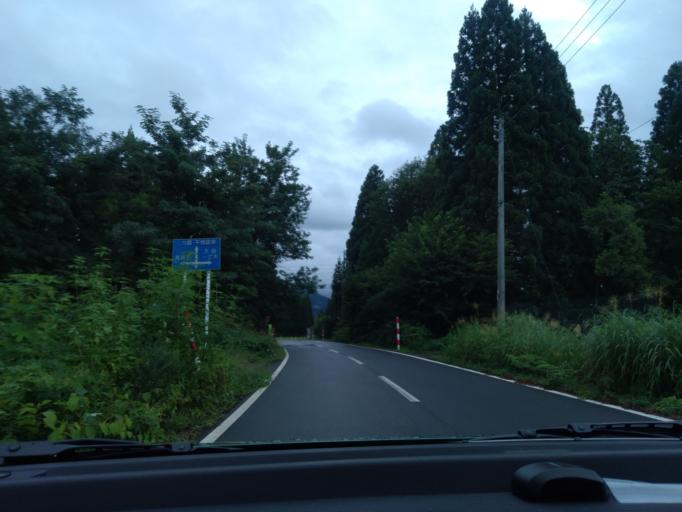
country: JP
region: Akita
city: Kakunodatemachi
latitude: 39.4669
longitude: 140.6215
